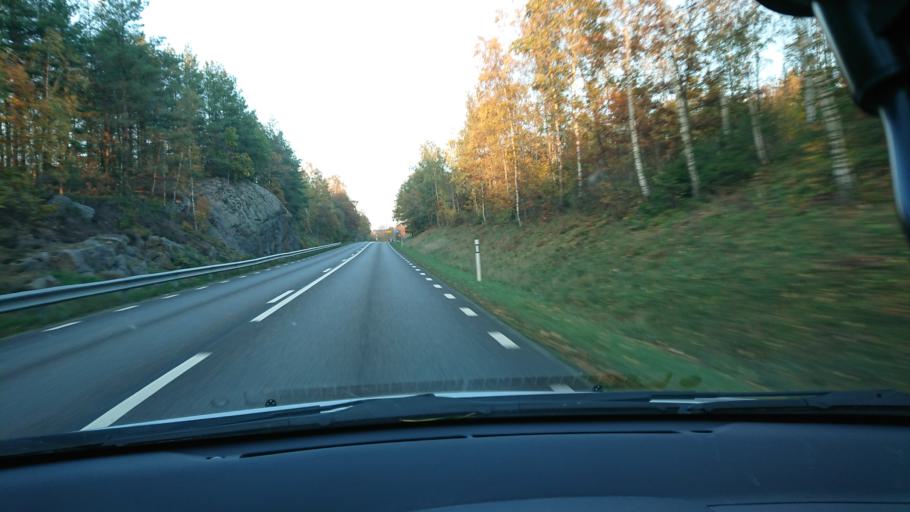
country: SE
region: Halland
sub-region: Halmstads Kommun
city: Aled
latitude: 56.7028
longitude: 13.0200
